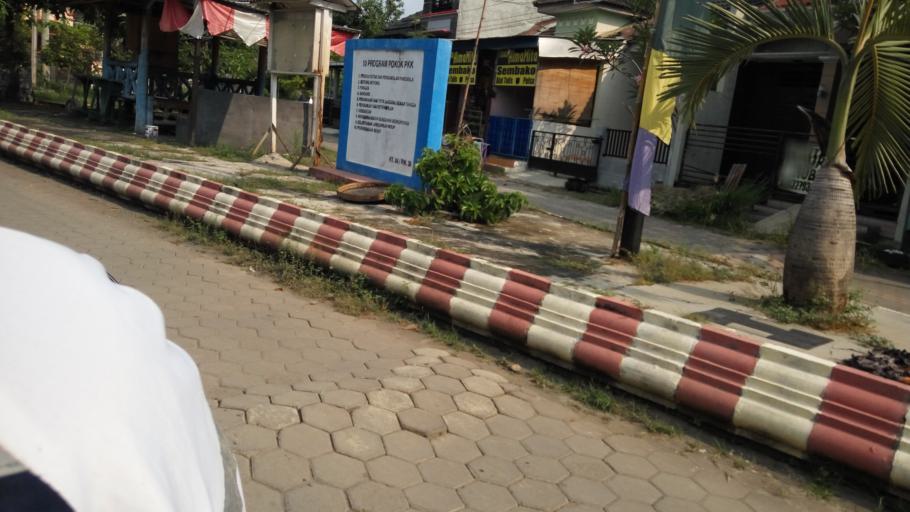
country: ID
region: Central Java
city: Mranggen
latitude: -7.0388
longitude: 110.4730
